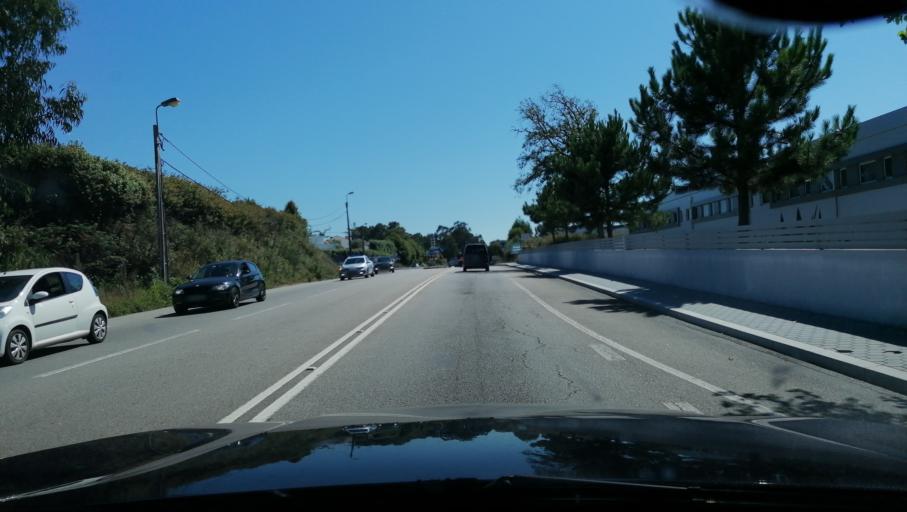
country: PT
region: Porto
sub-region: Vila Nova de Gaia
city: Gulpilhares
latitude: 41.0851
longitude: -8.6334
